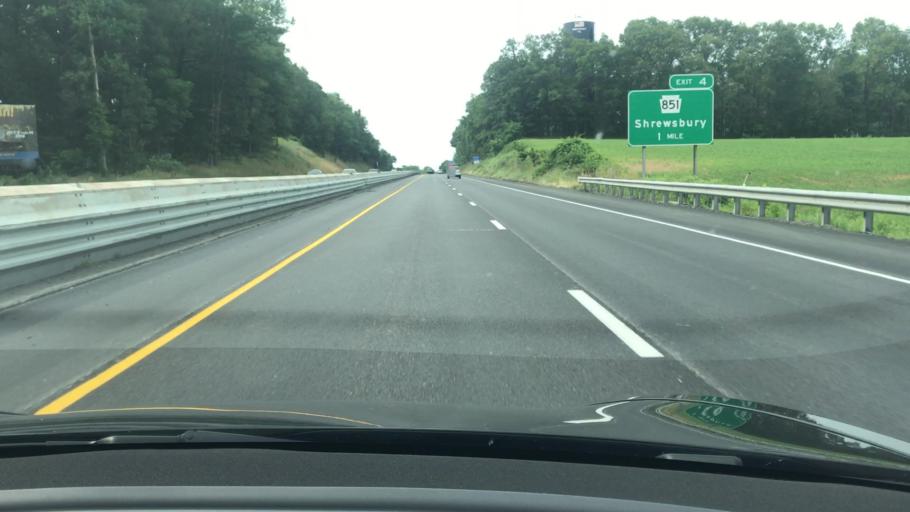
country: US
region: Pennsylvania
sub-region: York County
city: Shrewsbury
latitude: 39.7899
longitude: -76.6750
